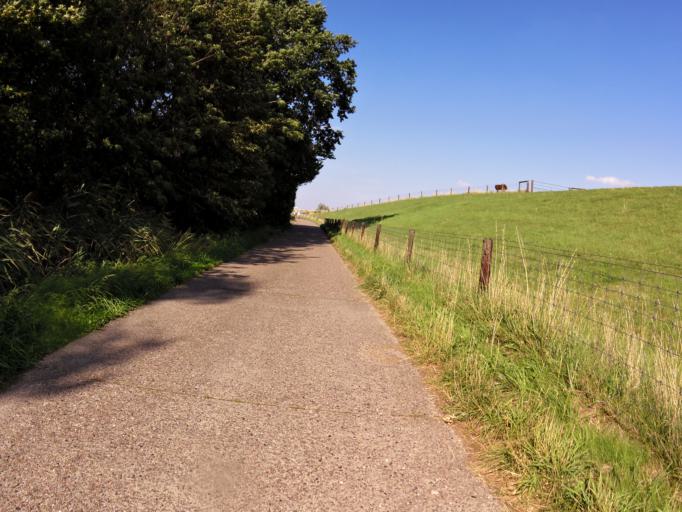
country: DE
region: Lower Saxony
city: Ovelgonne
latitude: 53.3832
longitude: 8.4587
